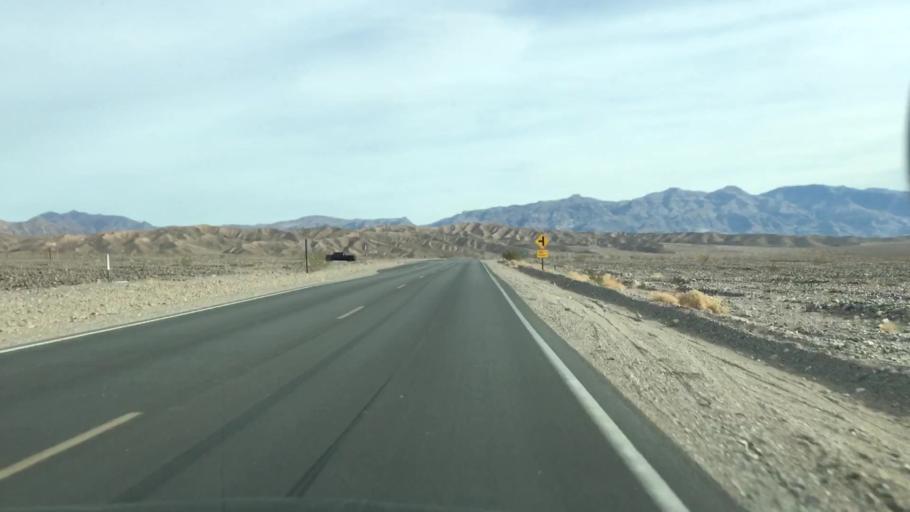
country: US
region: Nevada
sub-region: Nye County
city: Beatty
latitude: 36.6381
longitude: -117.0375
